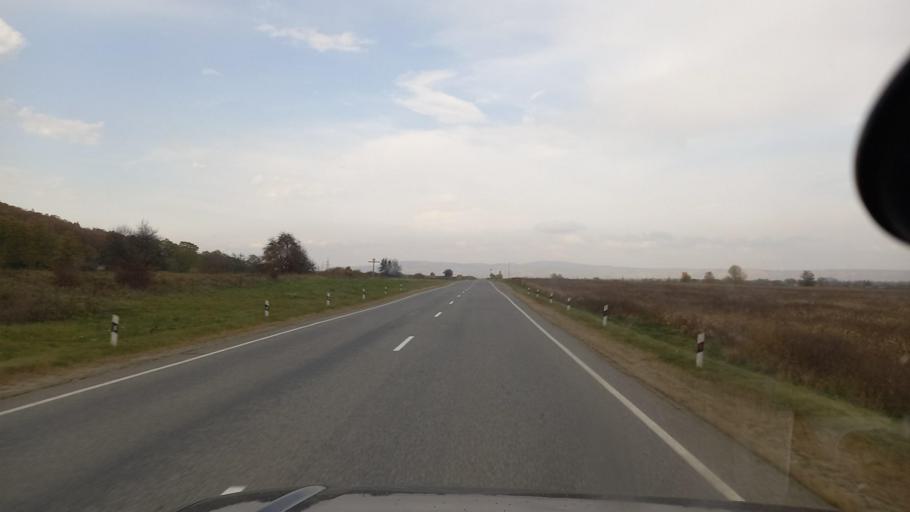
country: RU
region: Krasnodarskiy
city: Shedok
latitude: 44.2451
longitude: 40.8622
